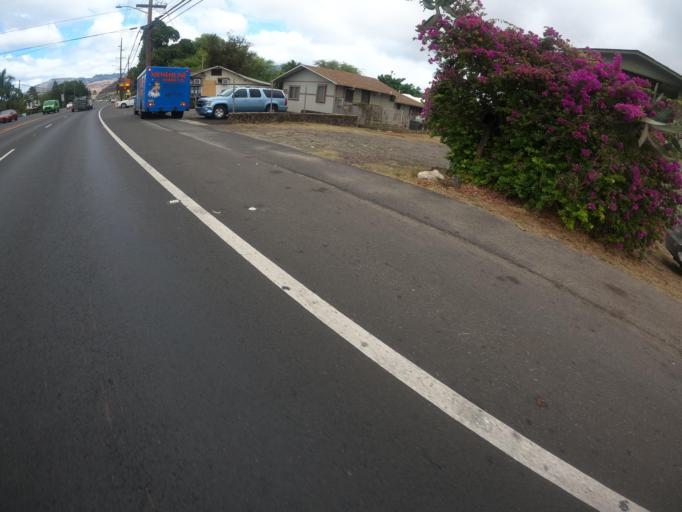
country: US
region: Hawaii
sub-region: Honolulu County
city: Ma'ili
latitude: 21.4061
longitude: -158.1772
